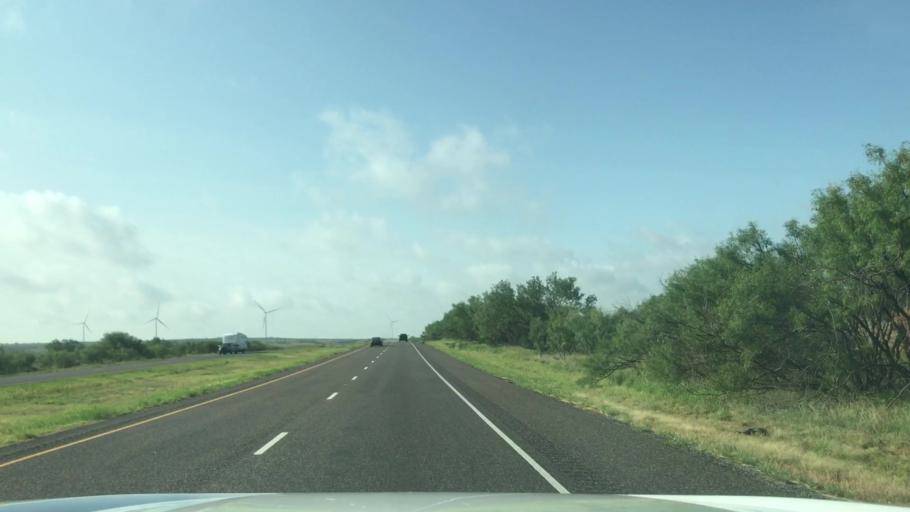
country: US
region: Texas
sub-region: Scurry County
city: Snyder
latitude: 32.9105
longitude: -101.0580
